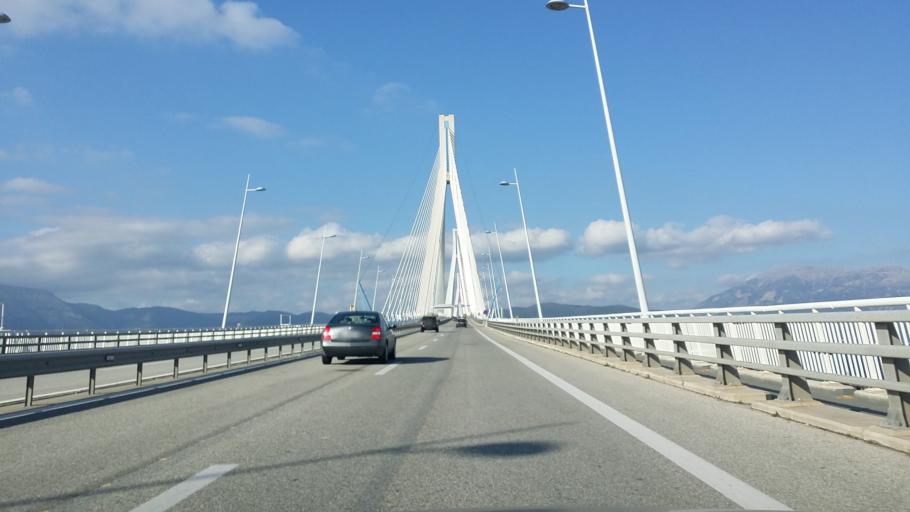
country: GR
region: West Greece
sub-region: Nomos Achaias
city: Rio
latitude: 38.3097
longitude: 21.7792
